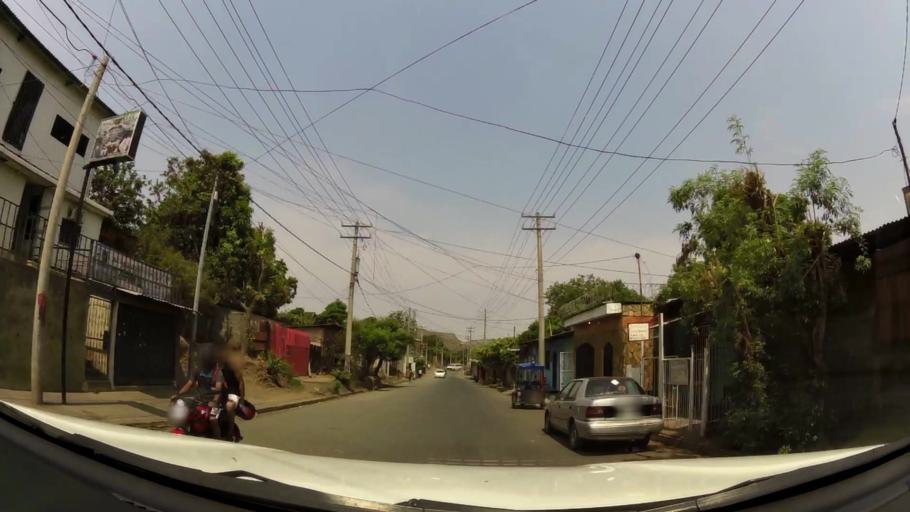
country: NI
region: Managua
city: Ciudad Sandino
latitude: 12.1590
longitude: -86.3077
